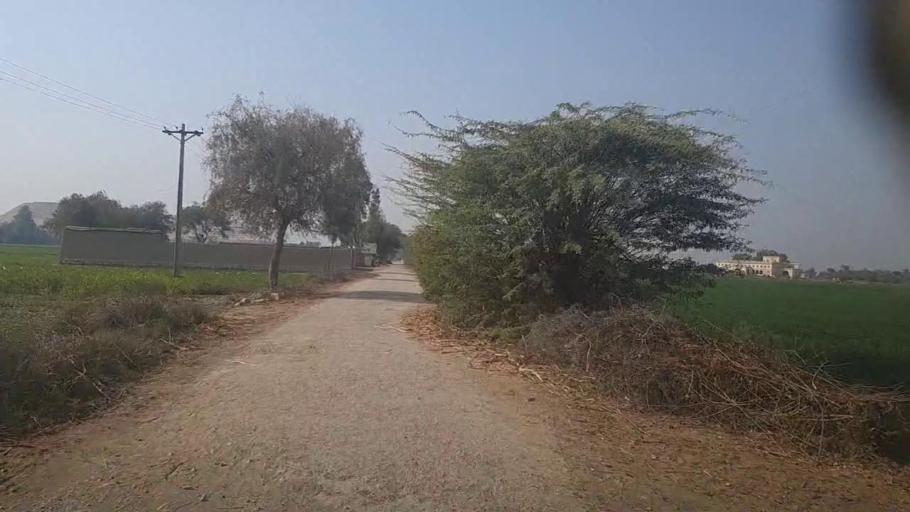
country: PK
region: Sindh
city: Kot Diji
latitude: 27.3478
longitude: 68.7241
